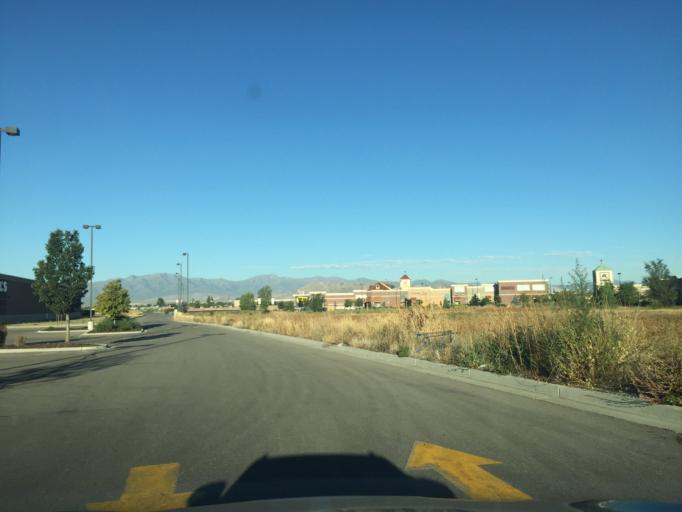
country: US
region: Utah
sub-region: Utah County
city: American Fork
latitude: 40.3834
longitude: -111.8159
